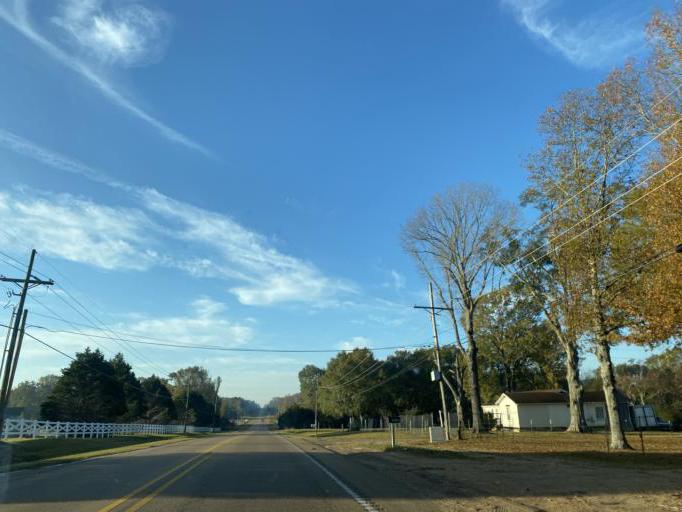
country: US
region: Mississippi
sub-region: Madison County
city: Madison
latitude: 32.5034
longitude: -90.0898
